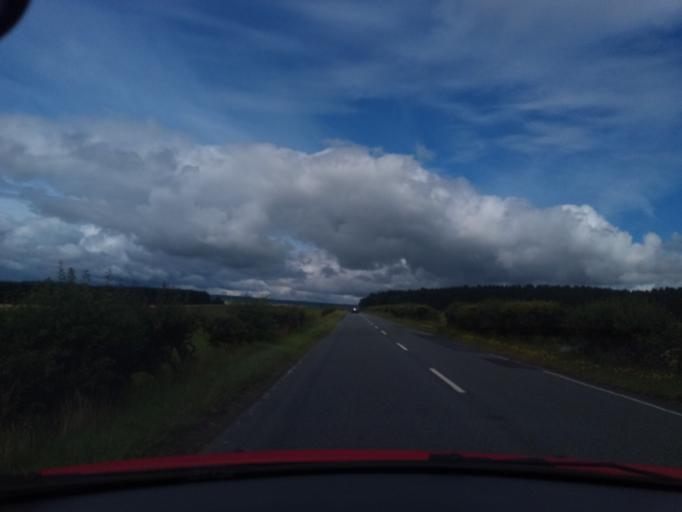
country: GB
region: Scotland
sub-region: The Scottish Borders
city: Lauder
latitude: 55.7314
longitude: -2.7325
